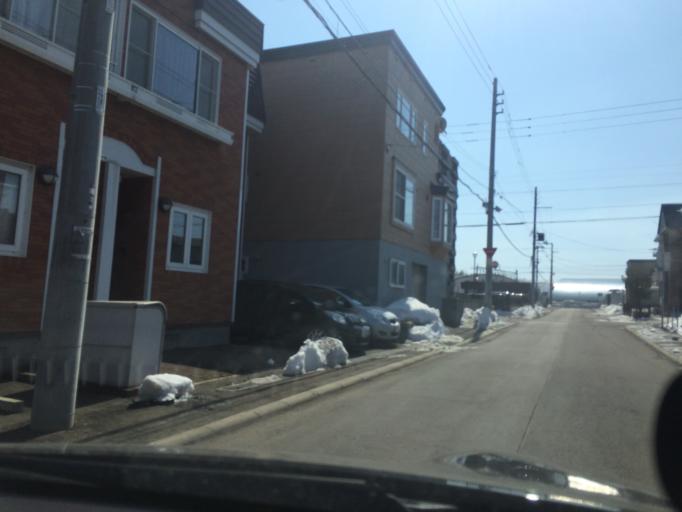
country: JP
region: Hokkaido
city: Sapporo
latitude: 43.0530
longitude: 141.4197
